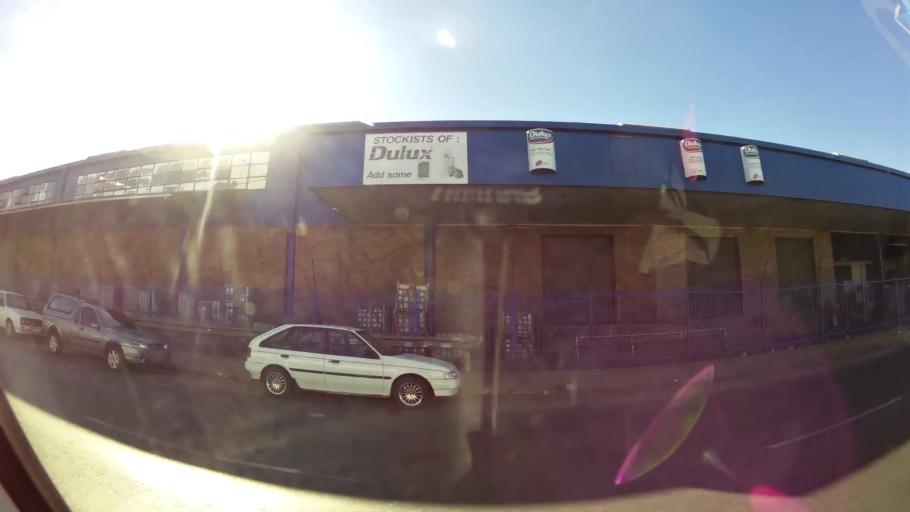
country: ZA
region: Limpopo
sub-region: Capricorn District Municipality
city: Polokwane
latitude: -23.9091
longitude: 29.4496
